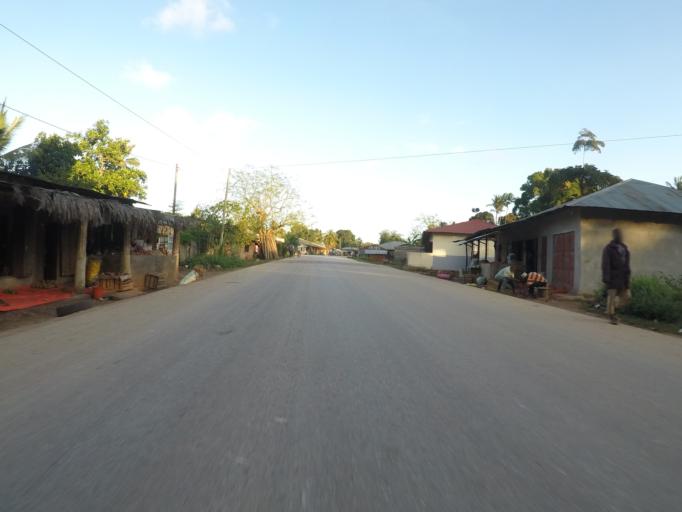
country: TZ
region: Zanzibar North
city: Gamba
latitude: -5.8846
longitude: 39.2857
